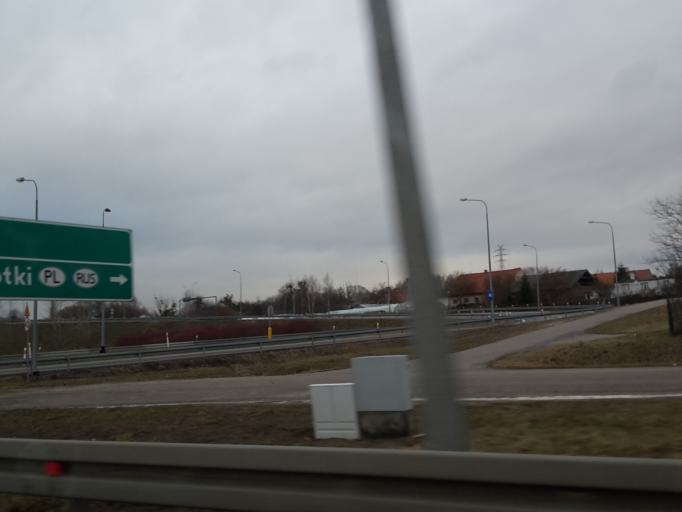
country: PL
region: Warmian-Masurian Voivodeship
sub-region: Powiat elblaski
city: Gronowo Gorne
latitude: 54.1372
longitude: 19.4515
